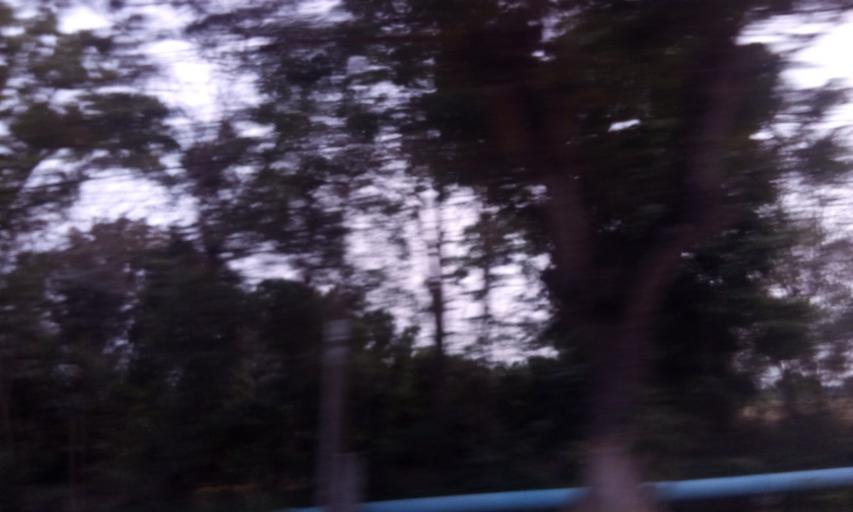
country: TH
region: Bangkok
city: Nong Chok
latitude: 13.8246
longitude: 100.9207
